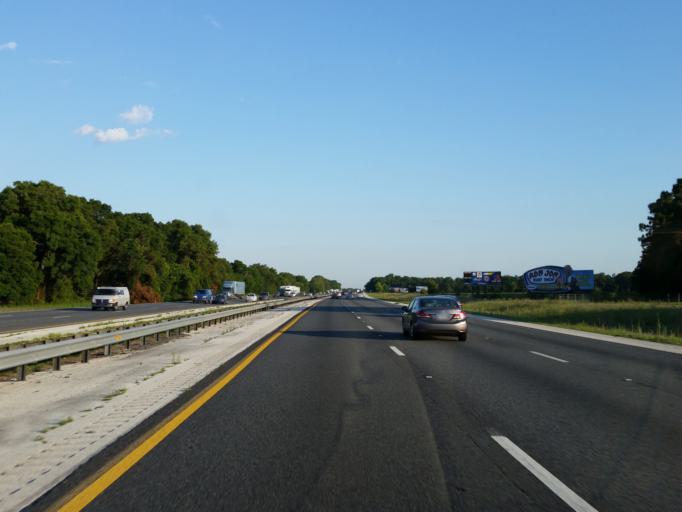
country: US
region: Florida
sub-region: Marion County
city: Belleview
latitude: 28.9683
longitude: -82.1283
